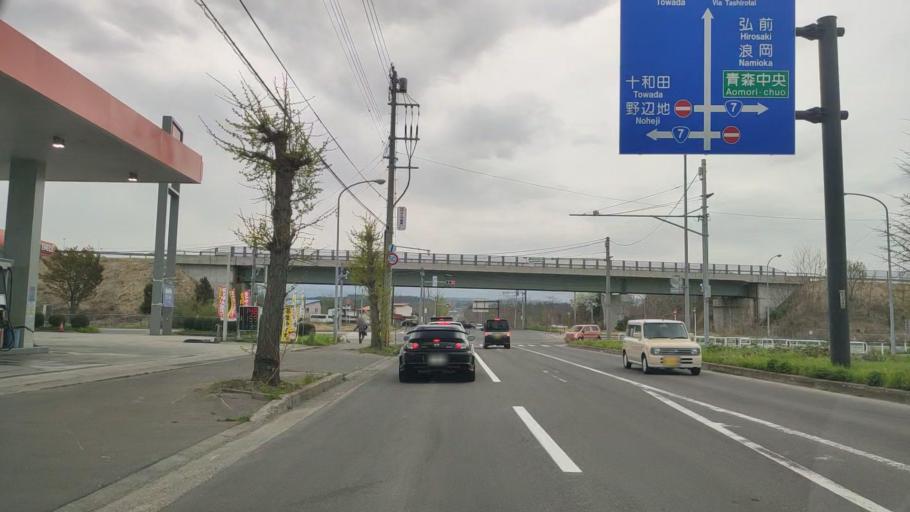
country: JP
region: Aomori
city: Aomori Shi
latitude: 40.7995
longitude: 140.7834
